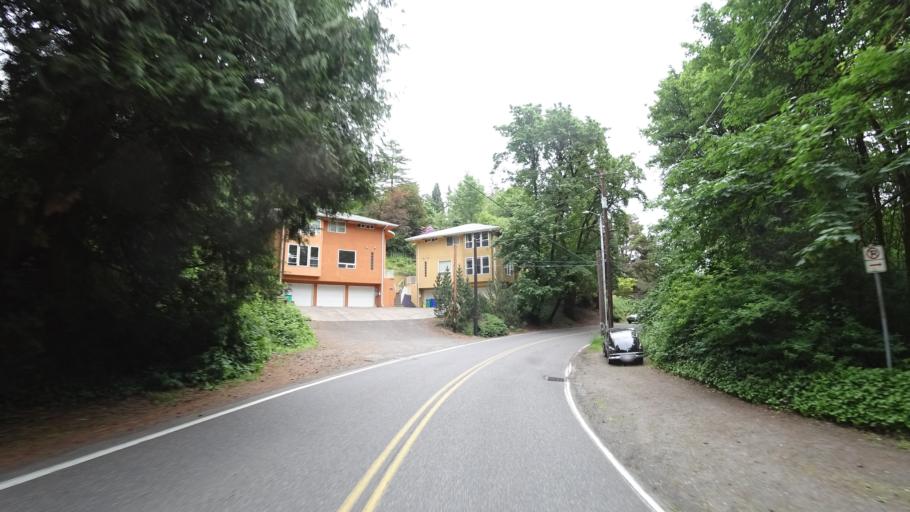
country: US
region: Oregon
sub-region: Multnomah County
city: Portland
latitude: 45.5062
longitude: -122.7004
